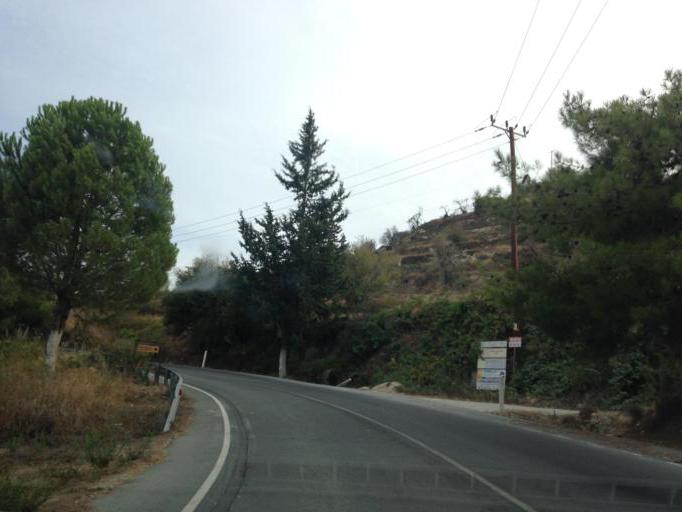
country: CY
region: Limassol
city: Pachna
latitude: 34.7839
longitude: 32.7958
